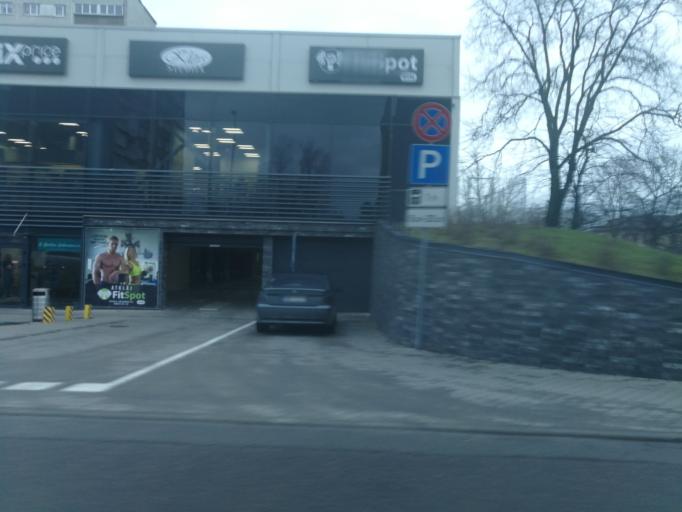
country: LV
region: Riga
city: Bolderaja
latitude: 57.0312
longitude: 24.1108
